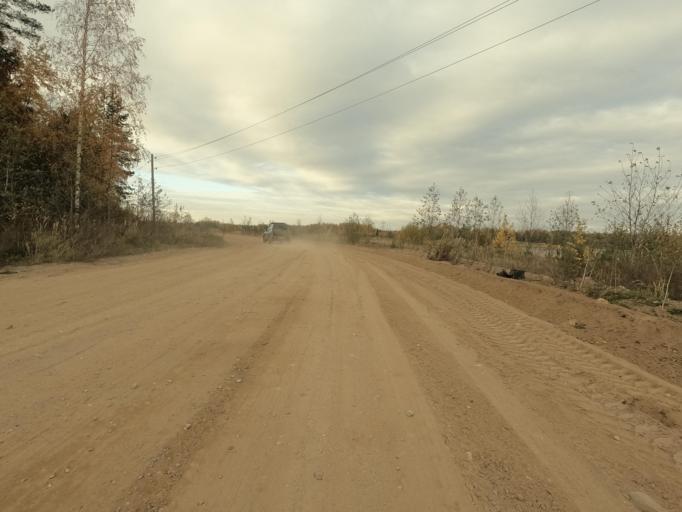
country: RU
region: Leningrad
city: Priladozhskiy
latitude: 59.7090
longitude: 31.3634
